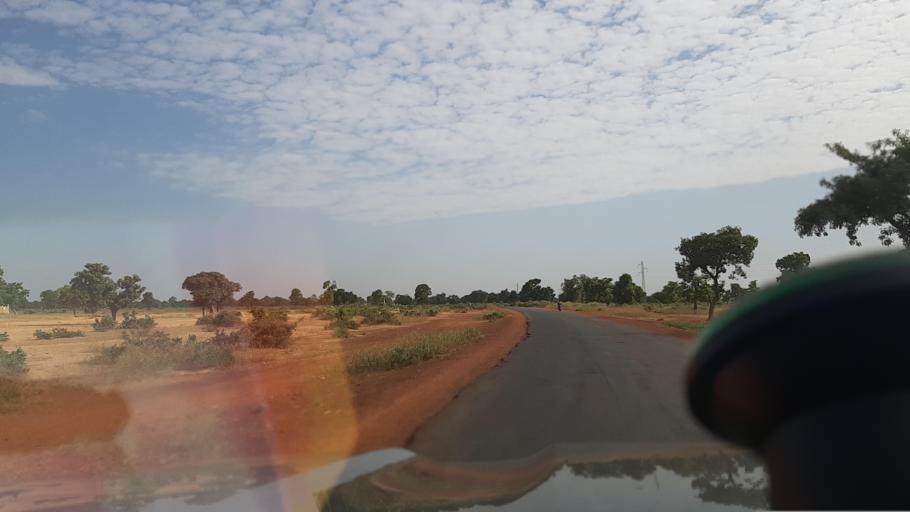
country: ML
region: Segou
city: Segou
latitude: 13.5010
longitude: -6.1509
